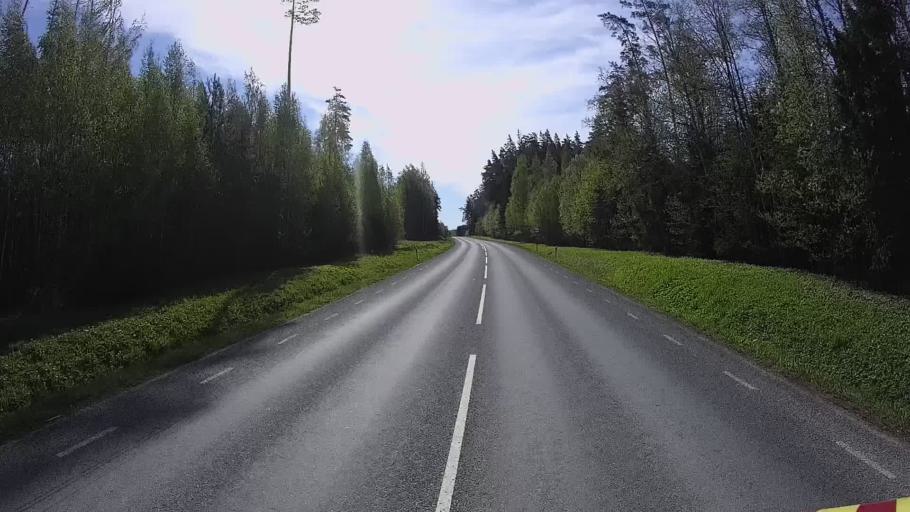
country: EE
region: Polvamaa
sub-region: Polva linn
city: Polva
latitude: 58.1645
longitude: 27.1512
